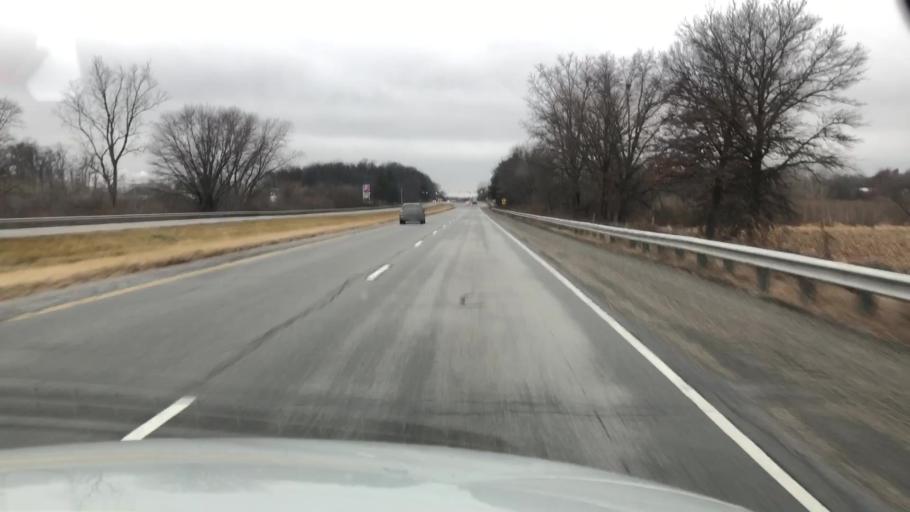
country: US
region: Indiana
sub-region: Whitley County
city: Churubusco
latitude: 41.1261
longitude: -85.3316
